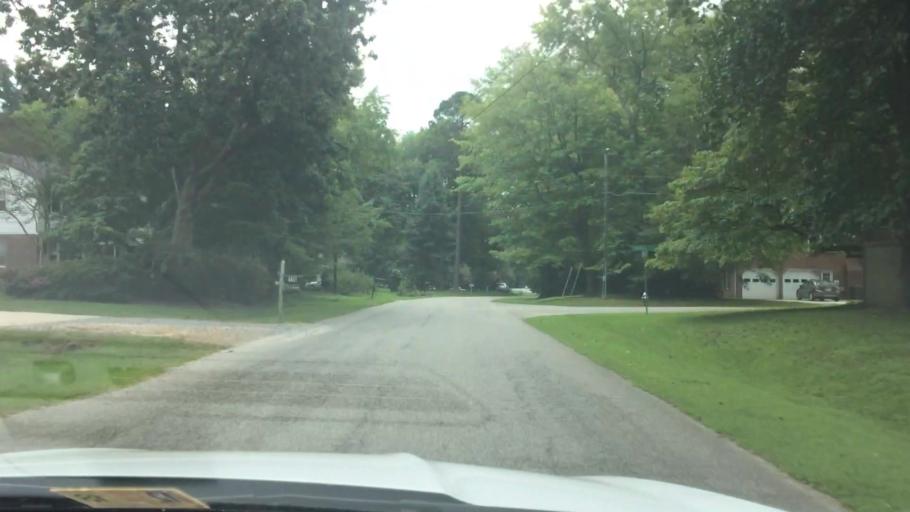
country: US
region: Virginia
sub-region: York County
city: Yorktown
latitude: 37.1719
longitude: -76.4419
